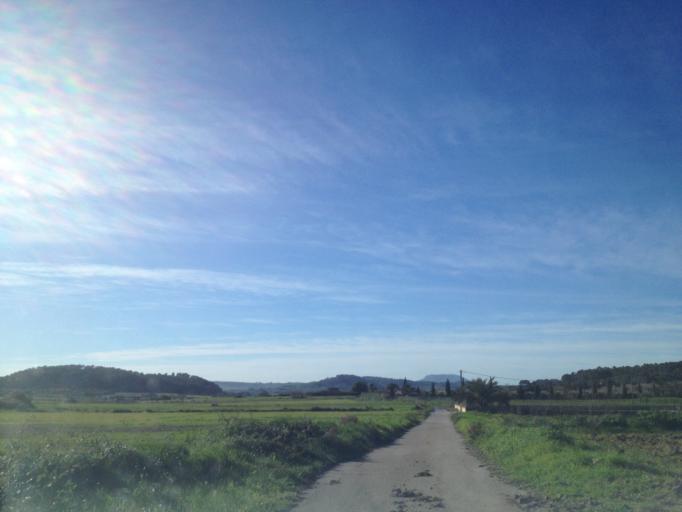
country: ES
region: Balearic Islands
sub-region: Illes Balears
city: Sineu
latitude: 39.6509
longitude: 3.0378
